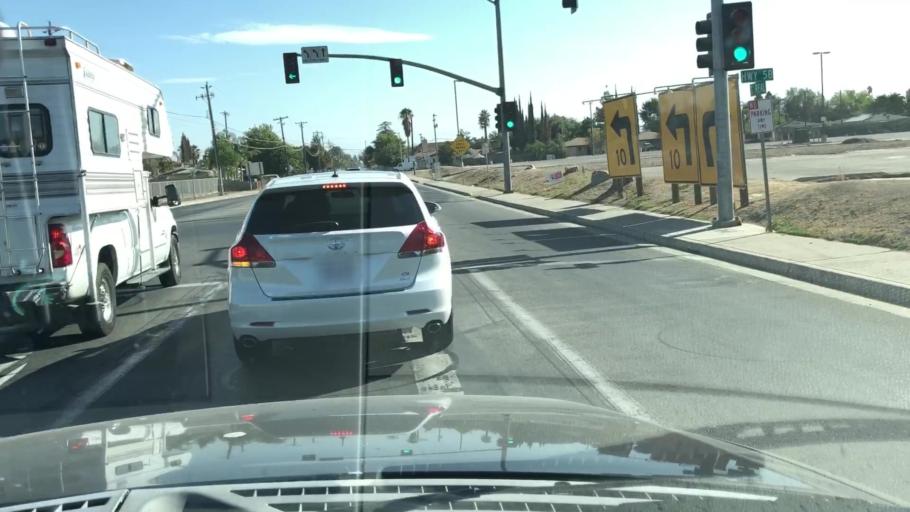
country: US
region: California
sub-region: Kern County
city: Bakersfield
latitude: 35.3530
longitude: -119.0435
